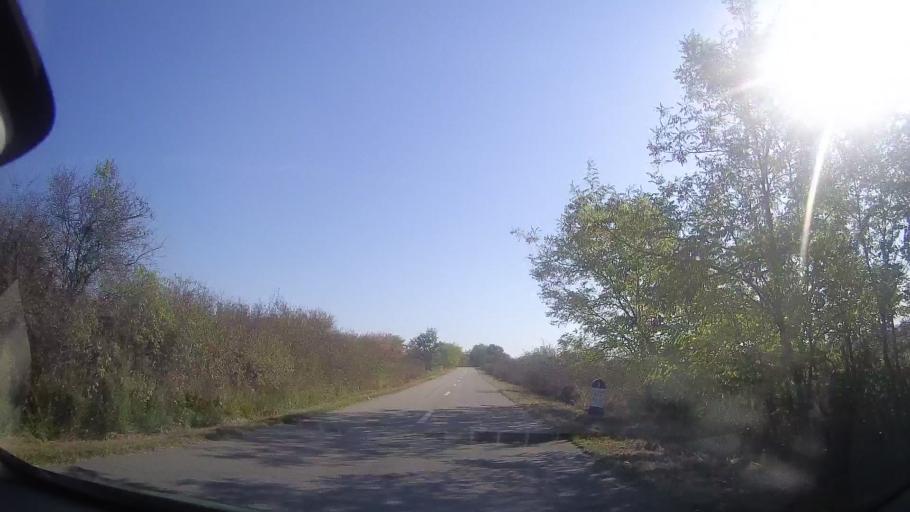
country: RO
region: Timis
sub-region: Comuna Ghizela
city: Ghizela
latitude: 45.8270
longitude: 21.7350
